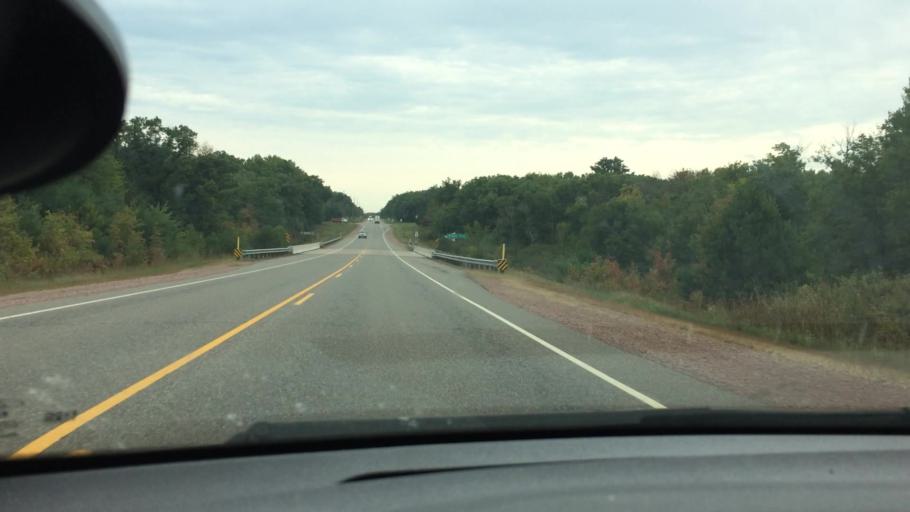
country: US
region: Wisconsin
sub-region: Clark County
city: Neillsville
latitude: 44.5699
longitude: -90.7264
